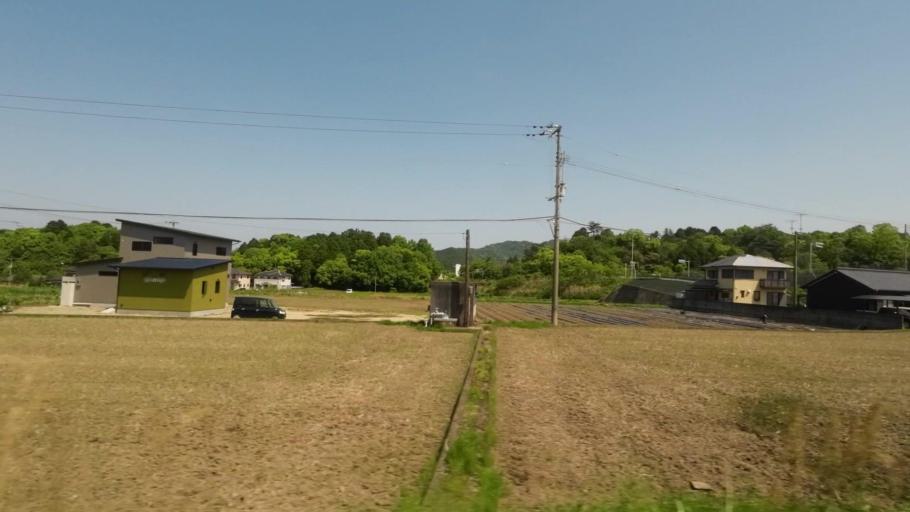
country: JP
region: Ehime
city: Saijo
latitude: 33.9221
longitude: 133.2267
